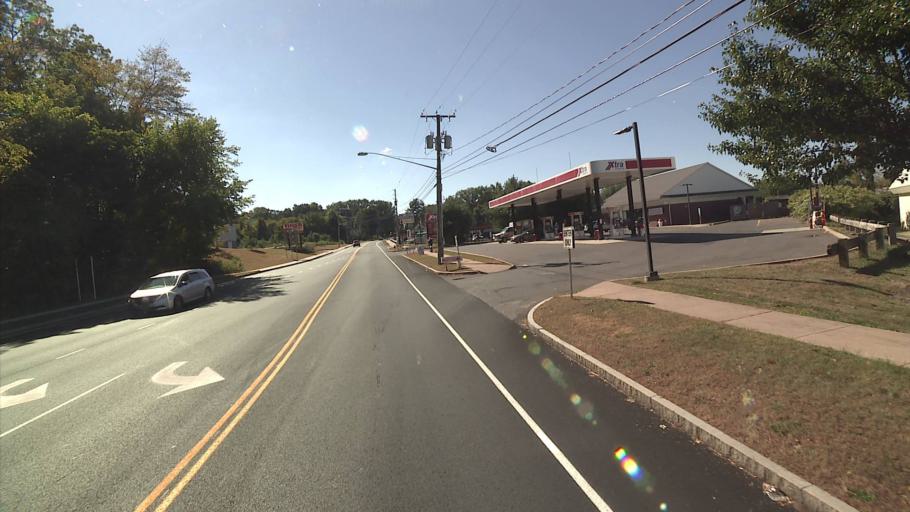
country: US
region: Connecticut
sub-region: Hartford County
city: Manchester
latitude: 41.8095
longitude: -72.5173
